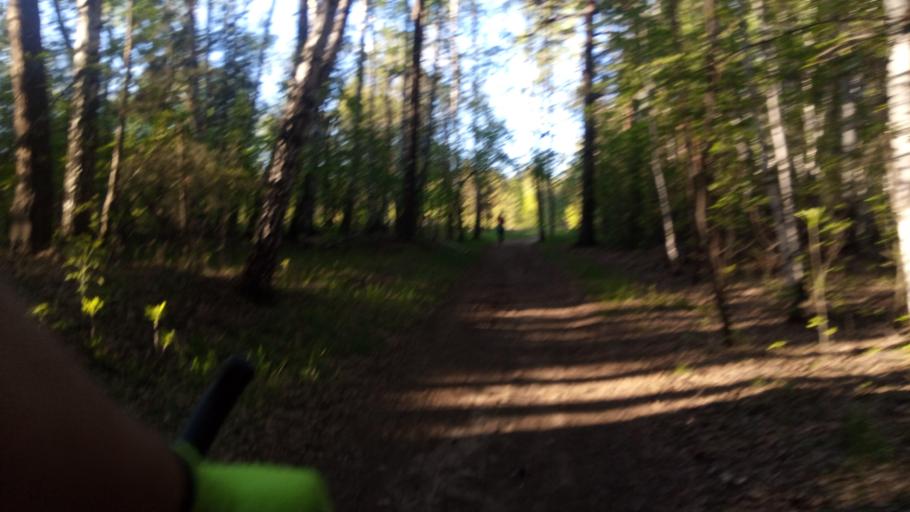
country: RU
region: Chelyabinsk
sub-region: Gorod Chelyabinsk
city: Chelyabinsk
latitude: 55.1514
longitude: 61.3360
